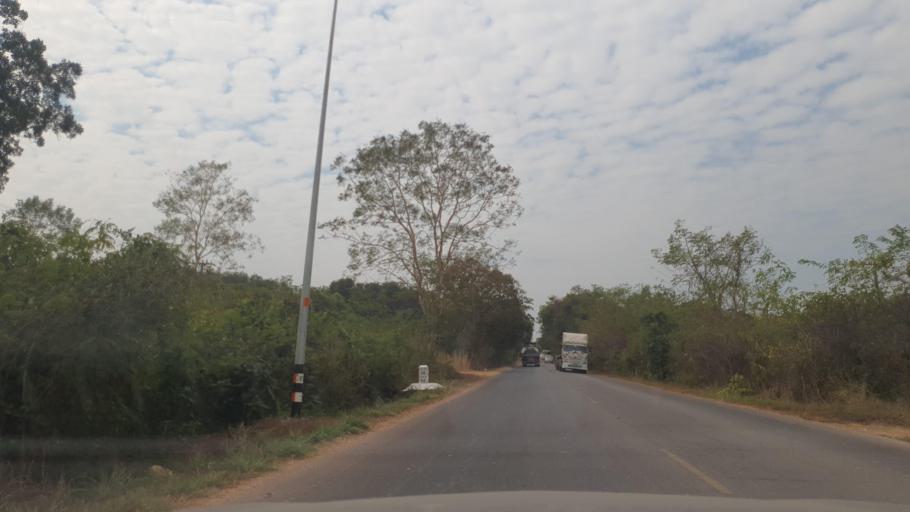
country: TH
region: Changwat Bueng Kan
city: Bung Khla
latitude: 18.3040
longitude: 103.9619
